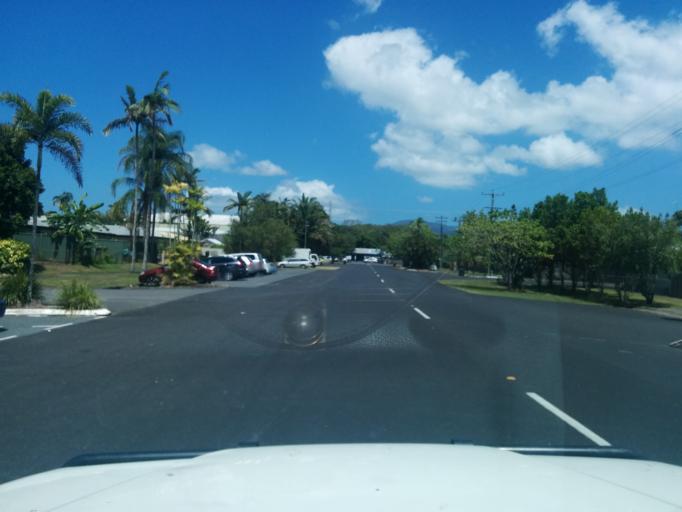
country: AU
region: Queensland
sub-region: Cairns
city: Cairns
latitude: -16.9119
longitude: 145.7482
